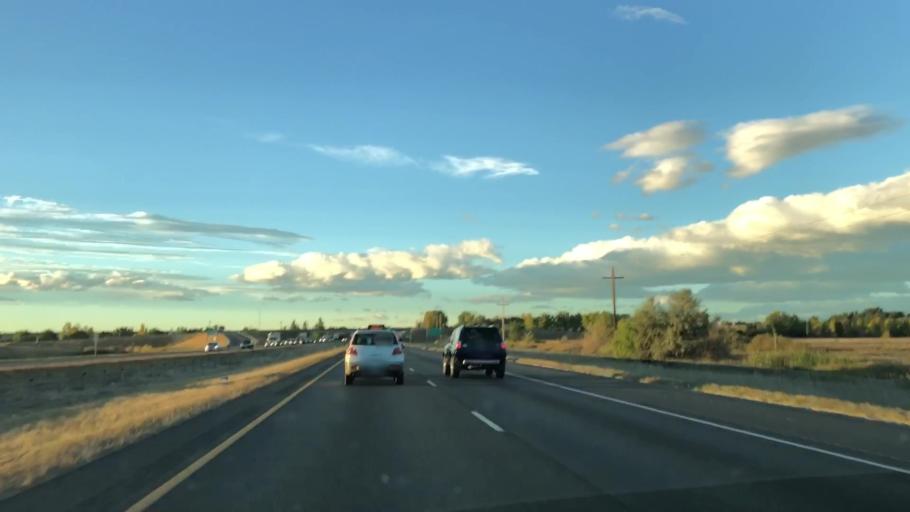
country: US
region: Colorado
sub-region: Weld County
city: Windsor
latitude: 40.5126
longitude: -104.9921
